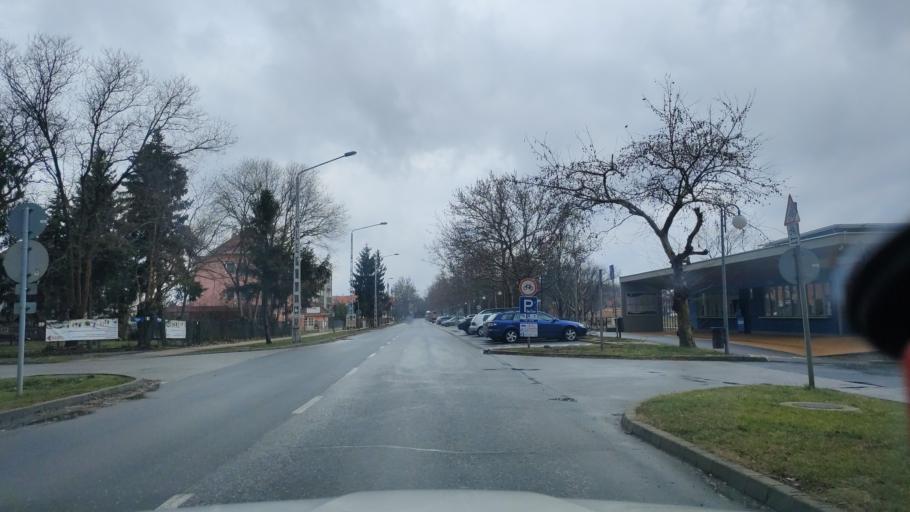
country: HU
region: Hajdu-Bihar
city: Hajduszoboszlo
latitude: 47.4510
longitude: 21.3965
